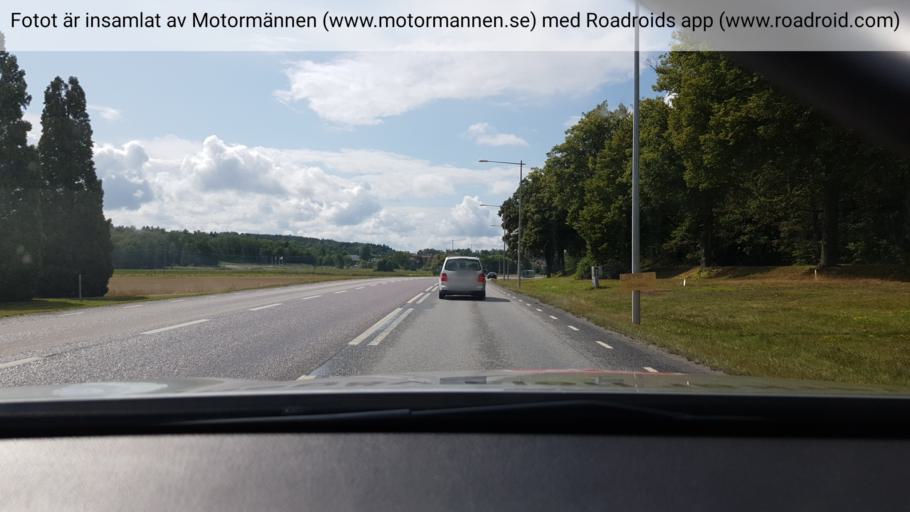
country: SE
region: Stockholm
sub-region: Ekero Kommun
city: Ekeroe
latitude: 59.2942
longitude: 17.8294
